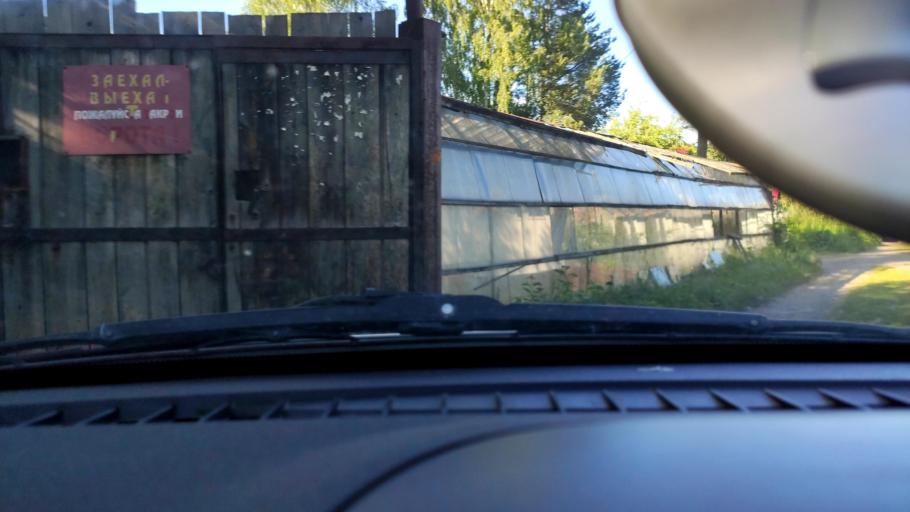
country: RU
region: Perm
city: Bershet'
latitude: 57.7003
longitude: 56.4067
